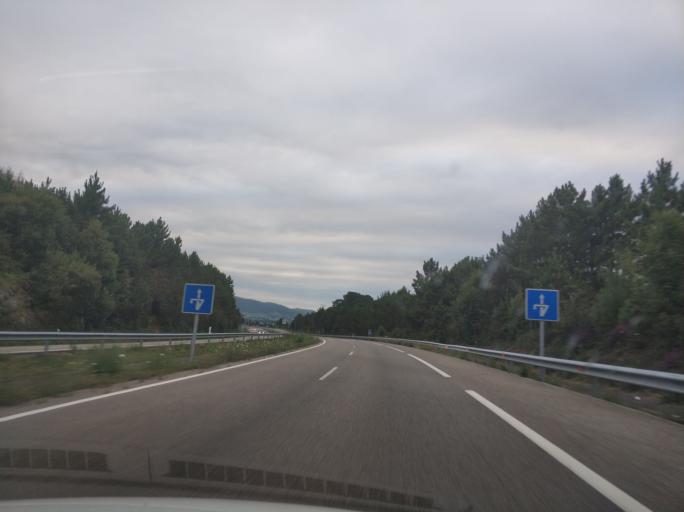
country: ES
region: Asturias
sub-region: Province of Asturias
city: Tineo
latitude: 43.5352
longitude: -6.4935
